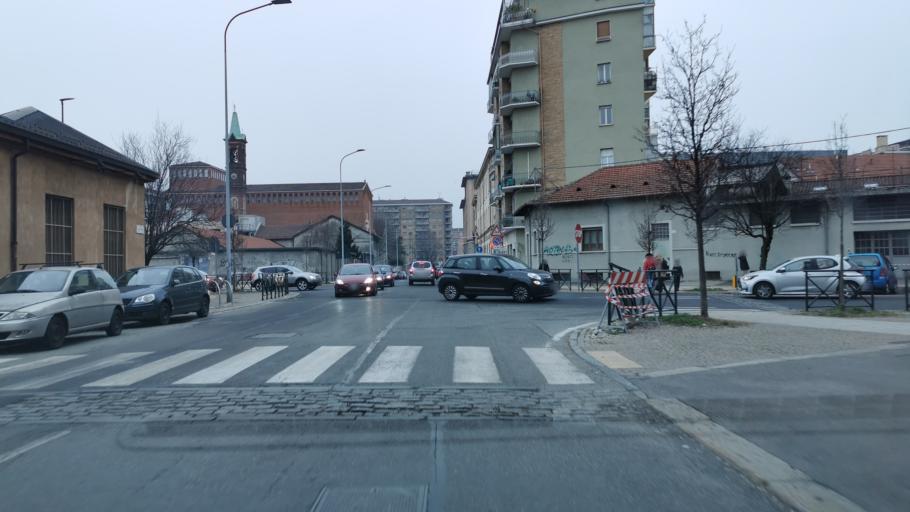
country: IT
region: Piedmont
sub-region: Provincia di Torino
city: Turin
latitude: 45.1036
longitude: 7.6676
